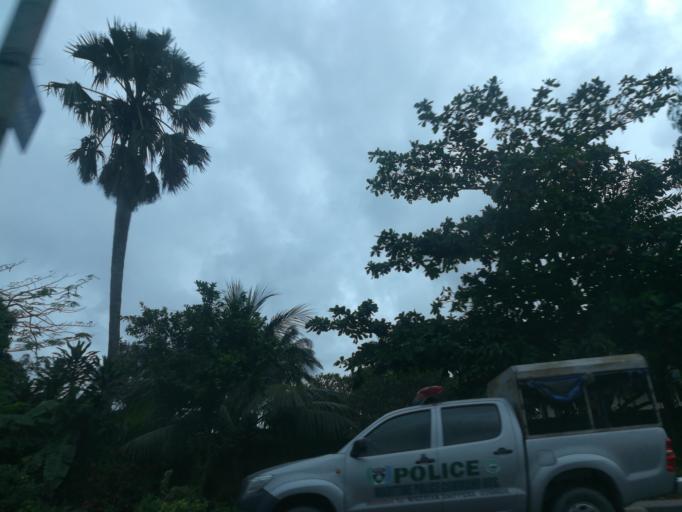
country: NG
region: Lagos
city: Ikoyi
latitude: 6.4525
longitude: 3.4489
